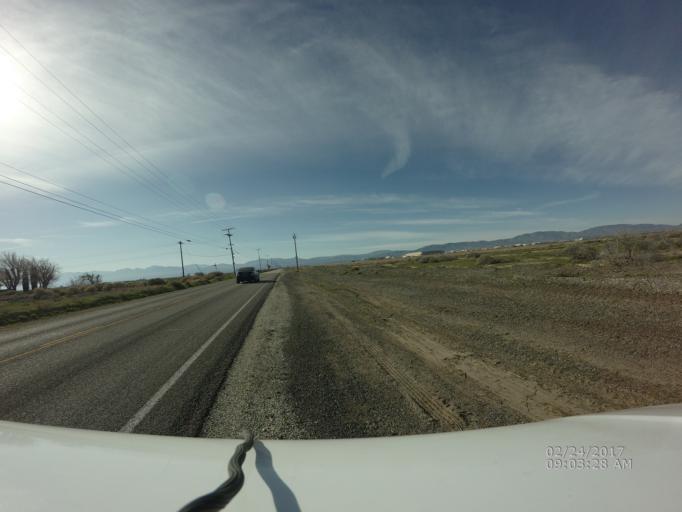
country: US
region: California
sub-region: Los Angeles County
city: Lancaster
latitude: 34.6614
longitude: -118.0589
